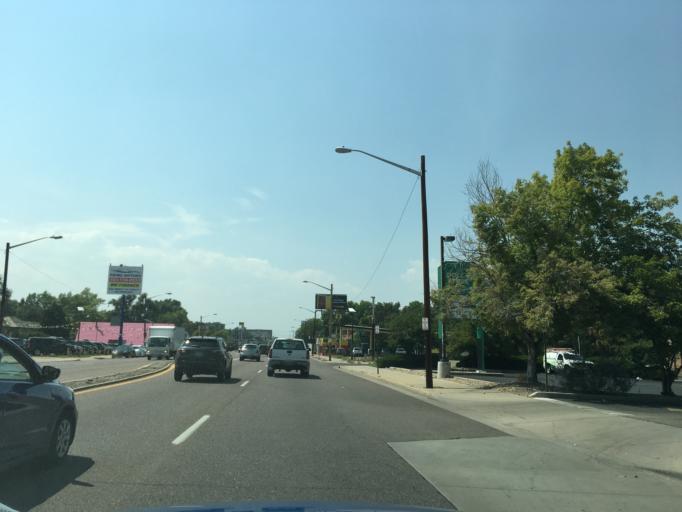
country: US
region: Colorado
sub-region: Arapahoe County
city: Glendale
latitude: 39.7402
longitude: -104.9301
